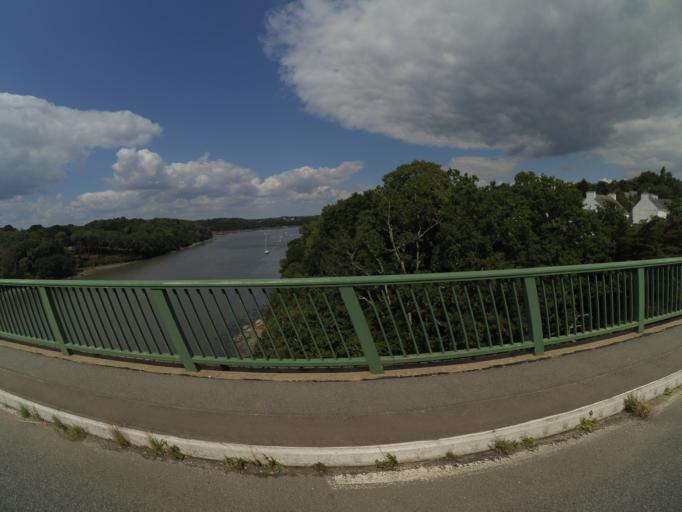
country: FR
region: Brittany
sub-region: Departement du Morbihan
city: Lanester
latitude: 47.7646
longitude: -3.3008
